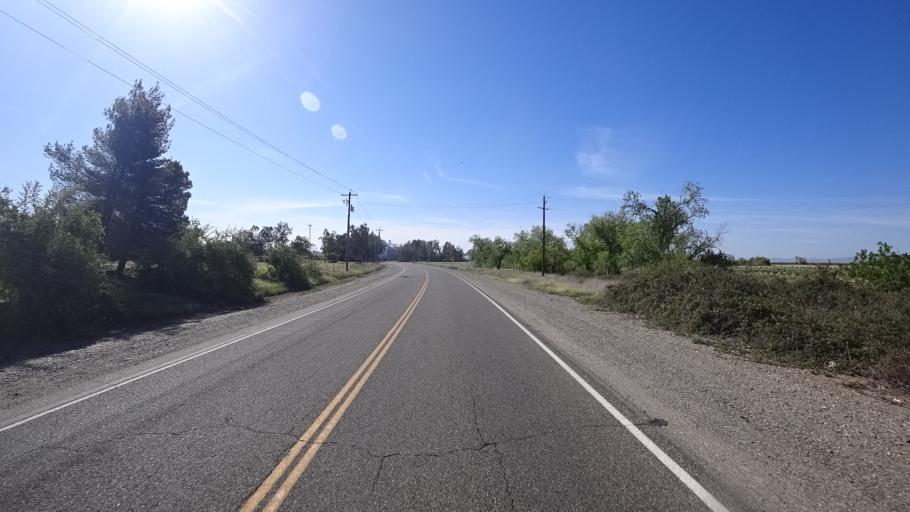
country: US
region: California
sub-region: Glenn County
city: Willows
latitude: 39.6260
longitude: -122.1969
